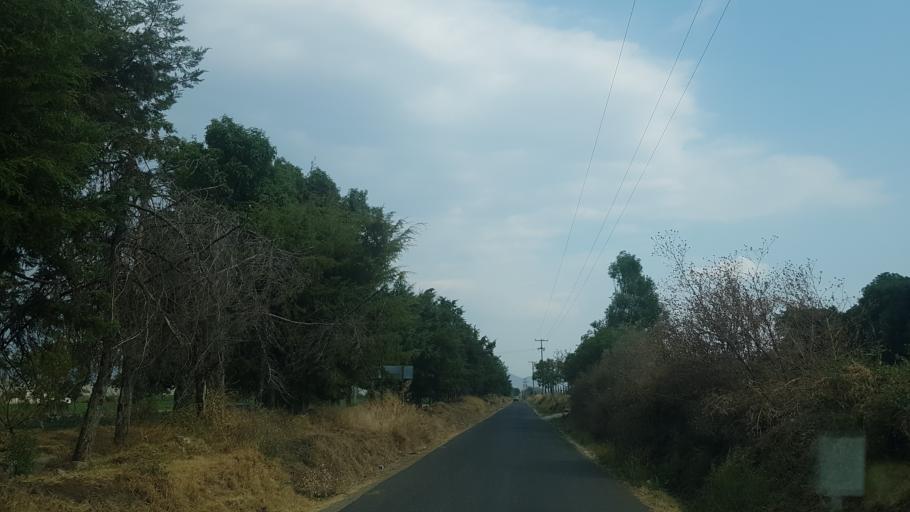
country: MX
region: Puebla
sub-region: Santa Isabel Cholula
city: Santa Ana Acozautla
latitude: 18.9577
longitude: -98.4031
